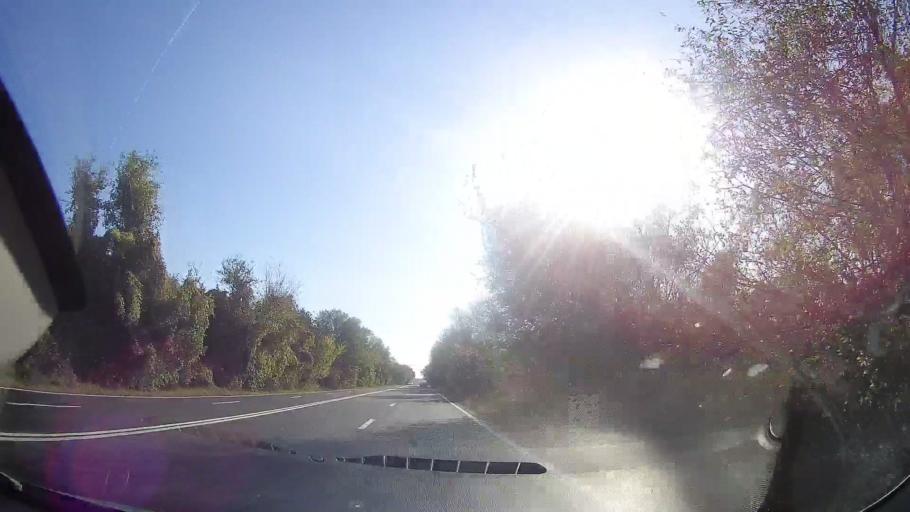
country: RO
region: Constanta
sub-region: Comuna Douazeci si Trei August
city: Dulcesti
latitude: 43.8652
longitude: 28.5751
